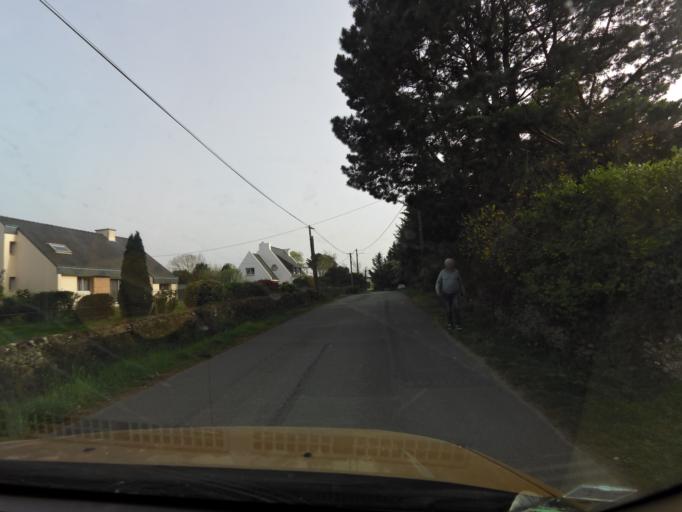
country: FR
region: Brittany
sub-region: Departement du Morbihan
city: Sene
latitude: 47.5794
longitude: -2.7135
